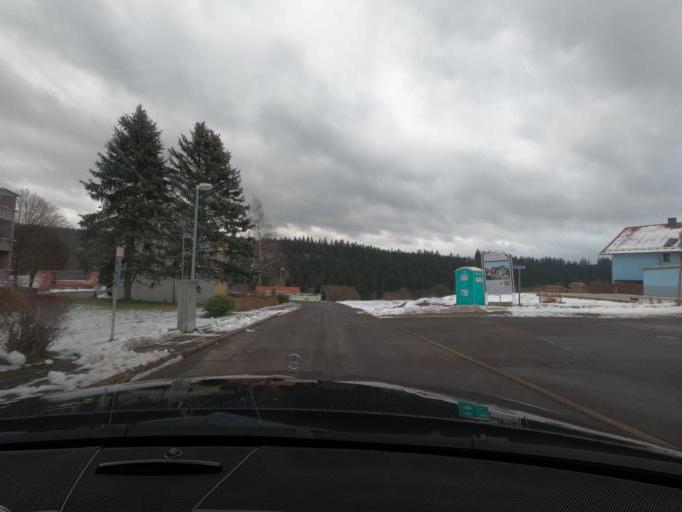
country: DE
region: Thuringia
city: Finsterbergen
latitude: 50.8325
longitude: 10.5946
